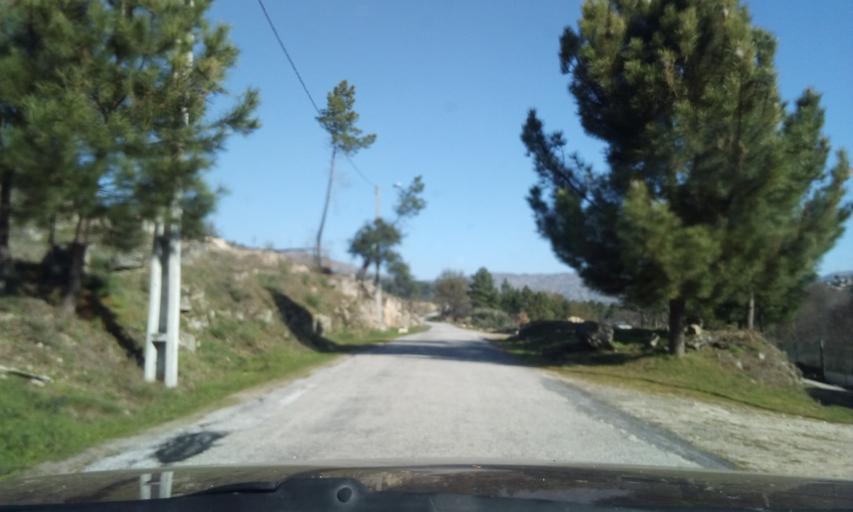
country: PT
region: Guarda
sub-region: Celorico da Beira
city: Celorico da Beira
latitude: 40.6825
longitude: -7.4554
